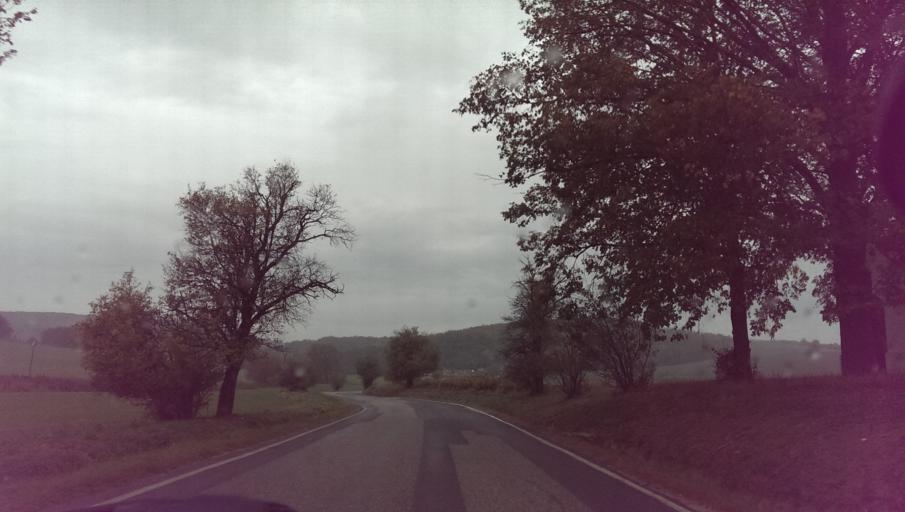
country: CZ
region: South Moravian
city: Ostopovice
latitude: 49.1443
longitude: 16.5461
